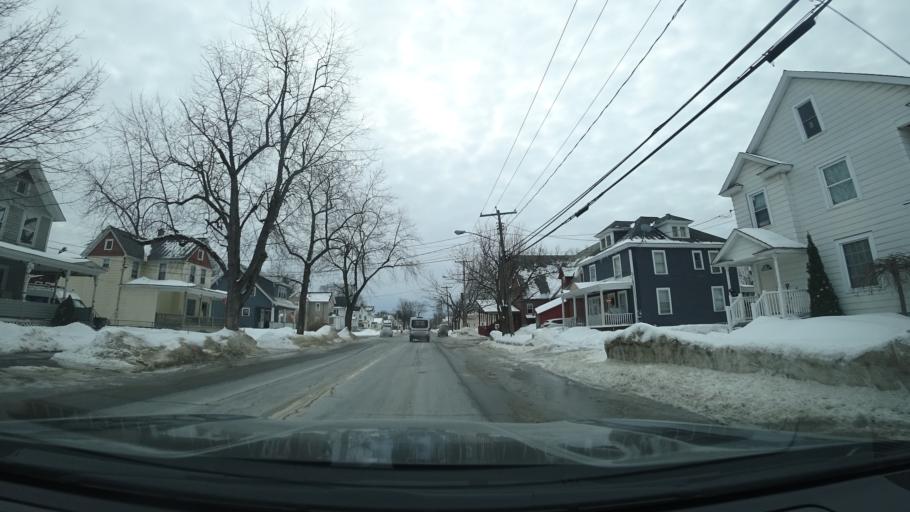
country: US
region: New York
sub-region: Saratoga County
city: South Glens Falls
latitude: 43.2979
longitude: -73.6341
